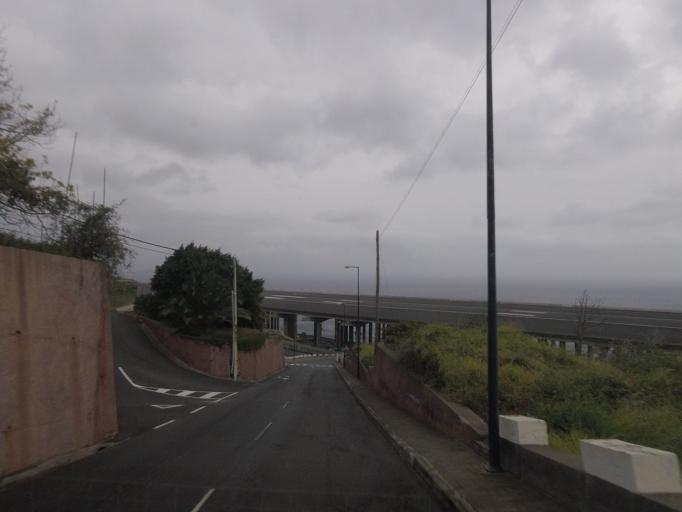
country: PT
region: Madeira
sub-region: Machico
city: Machico
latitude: 32.7030
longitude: -16.7727
